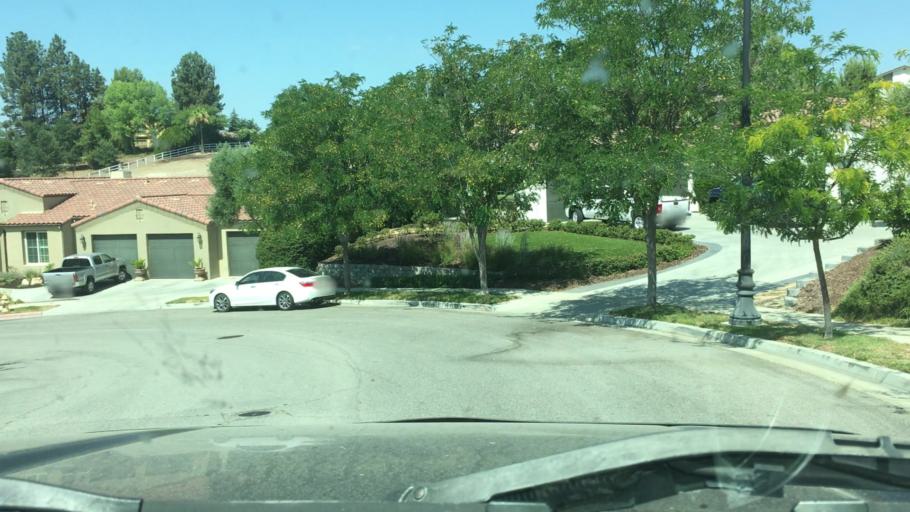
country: US
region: California
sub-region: San Luis Obispo County
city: Paso Robles
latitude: 35.6282
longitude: -120.6606
